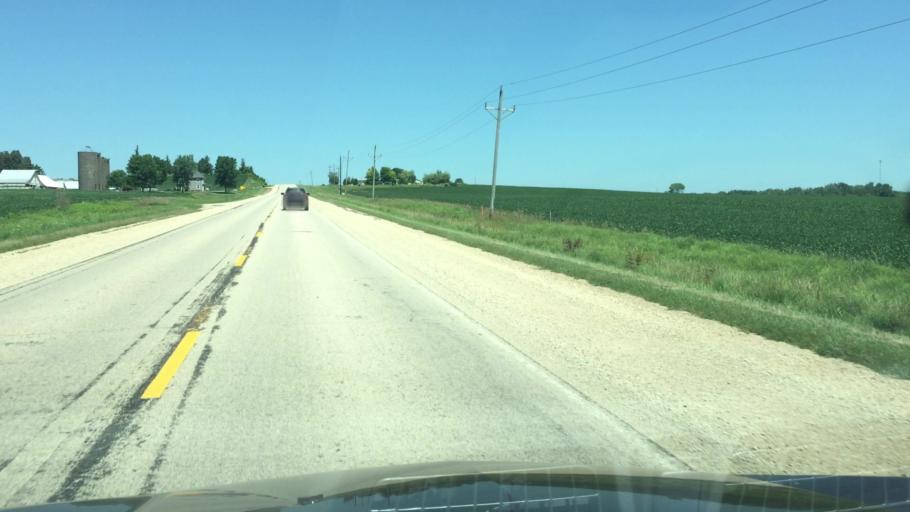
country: US
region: Iowa
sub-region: Cedar County
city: Mechanicsville
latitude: 41.9771
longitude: -91.1417
